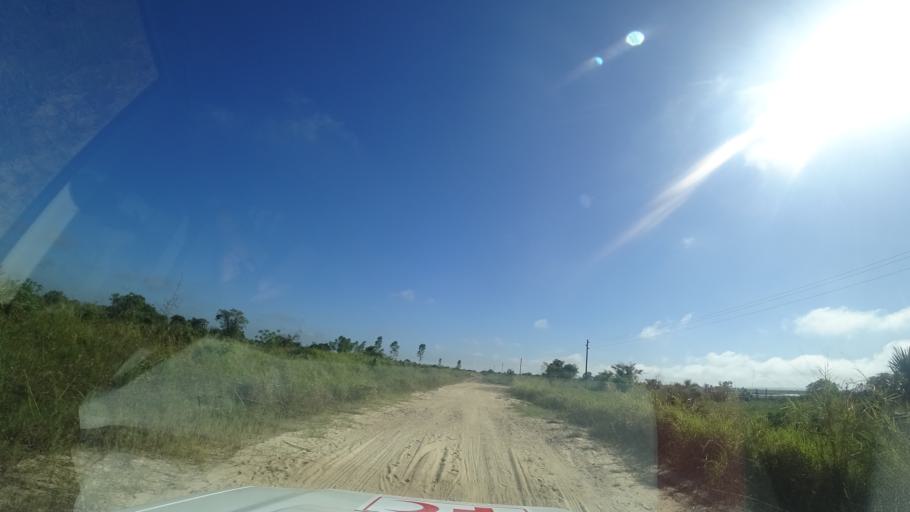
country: MZ
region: Sofala
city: Dondo
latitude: -19.4299
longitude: 34.5607
